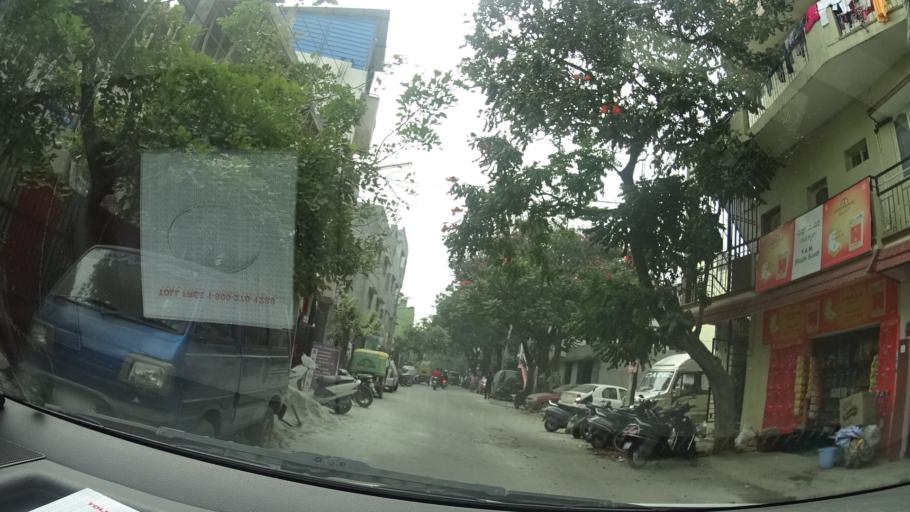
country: IN
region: Karnataka
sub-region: Bangalore Urban
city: Bangalore
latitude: 13.0221
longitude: 77.6259
